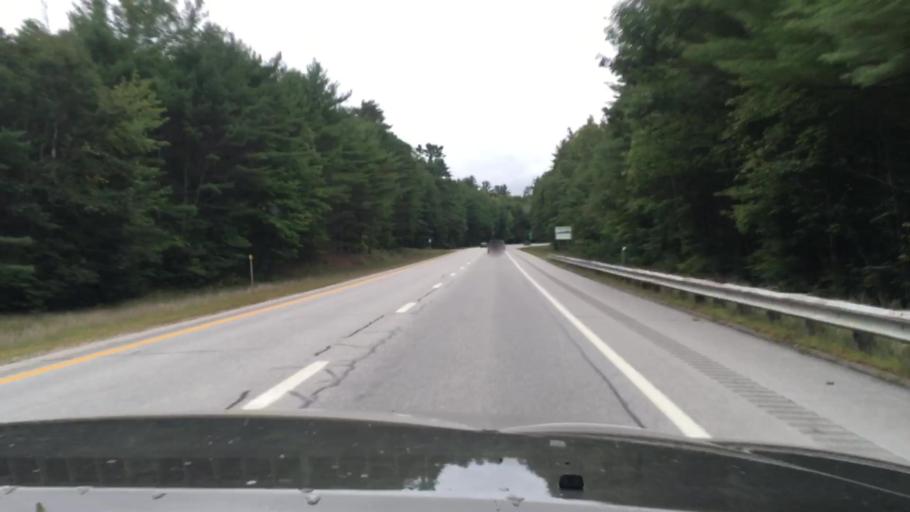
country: US
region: New Hampshire
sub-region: Belknap County
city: Sanbornton
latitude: 43.5186
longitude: -71.6169
